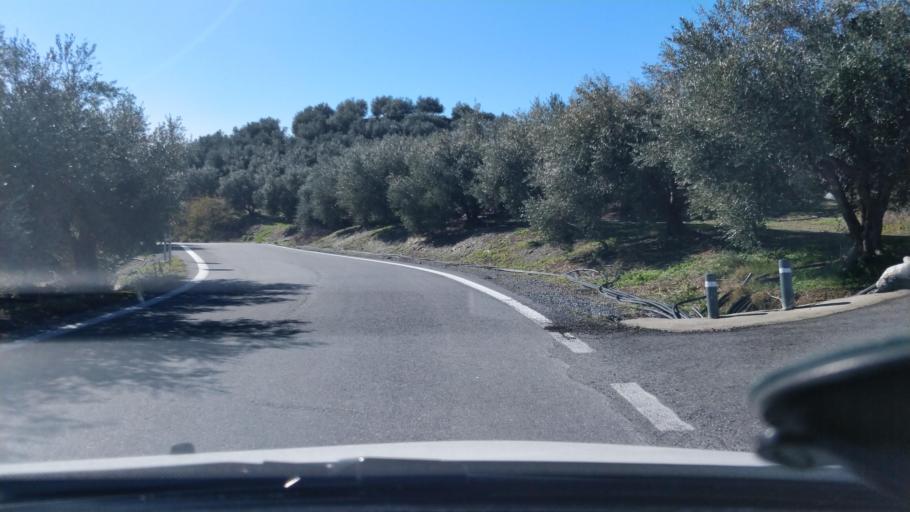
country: GR
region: Crete
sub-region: Nomos Irakleiou
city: Arkalochori
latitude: 35.0088
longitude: 25.4421
